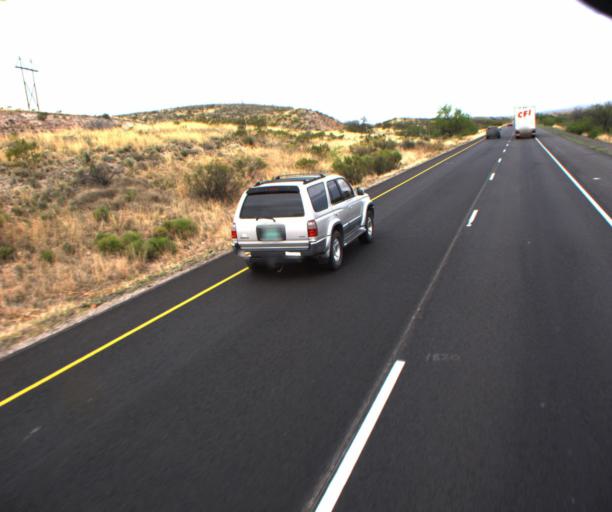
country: US
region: Arizona
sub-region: Cochise County
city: Mescal
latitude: 31.9679
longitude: -110.4671
